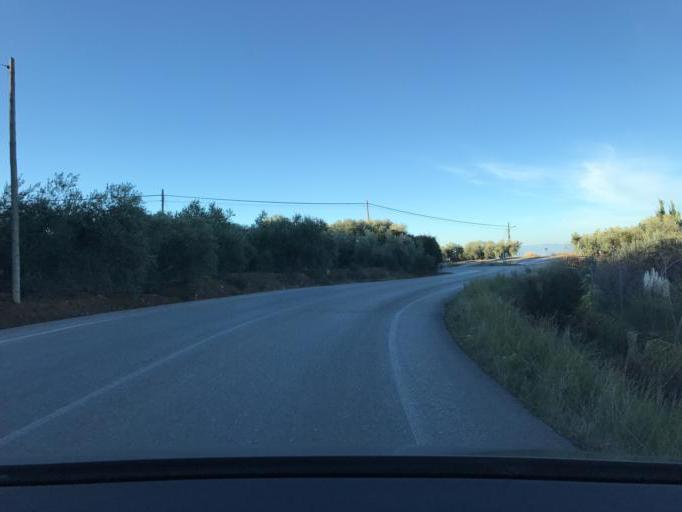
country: ES
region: Andalusia
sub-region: Provincia de Granada
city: Guevejar
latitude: 37.2621
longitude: -3.5881
